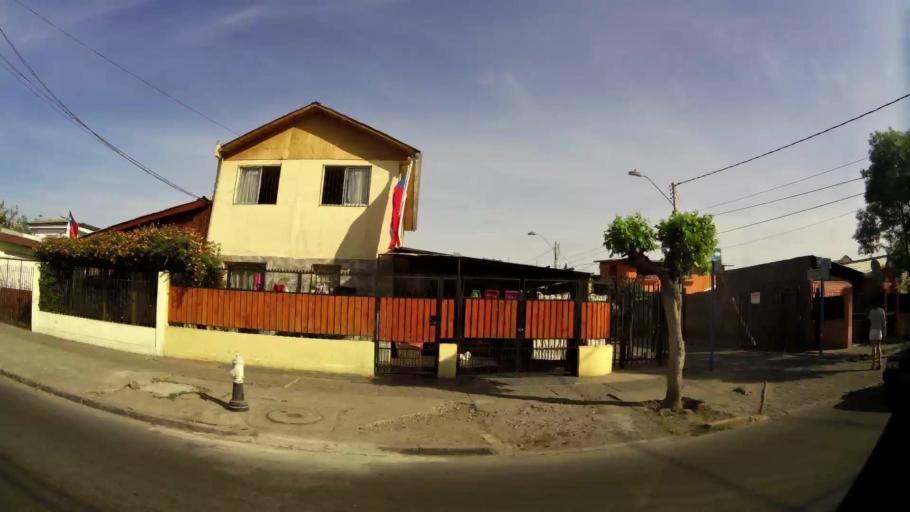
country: CL
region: Santiago Metropolitan
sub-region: Provincia de Santiago
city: La Pintana
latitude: -33.5208
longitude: -70.6324
